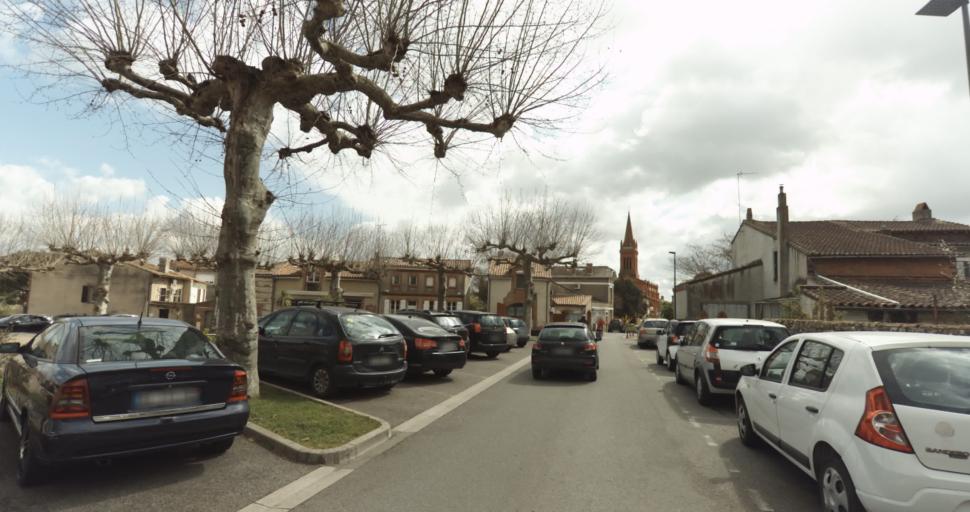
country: FR
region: Midi-Pyrenees
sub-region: Departement de la Haute-Garonne
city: Auterive
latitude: 43.3514
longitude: 1.4720
